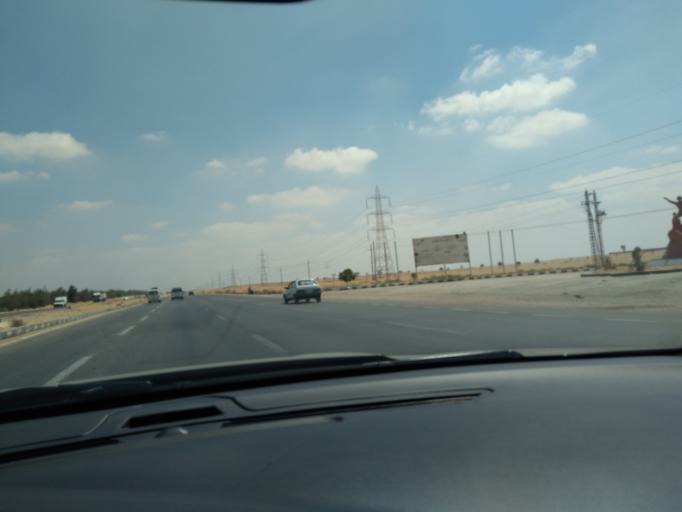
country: EG
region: Al Isma'iliyah
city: At Tall al Kabir
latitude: 30.3915
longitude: 31.9675
